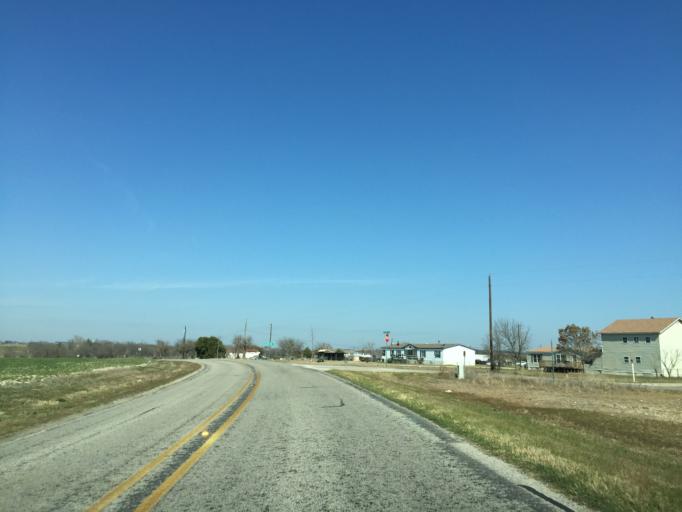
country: US
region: Texas
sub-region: Williamson County
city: Serenada
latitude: 30.6892
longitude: -97.5852
